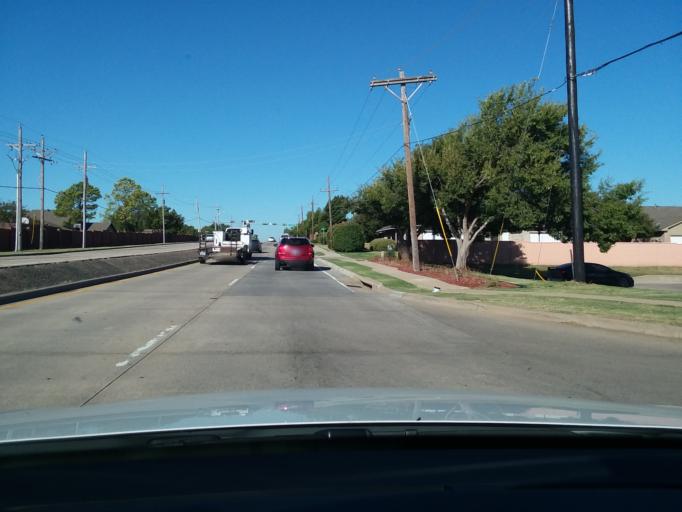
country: US
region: Texas
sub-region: Denton County
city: Highland Village
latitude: 33.0716
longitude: -97.0385
